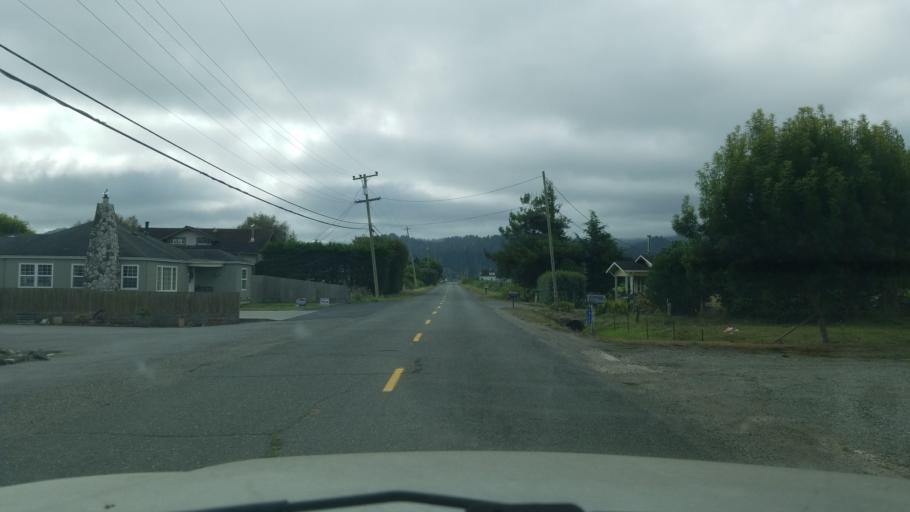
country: US
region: California
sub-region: Humboldt County
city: Ferndale
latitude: 40.5936
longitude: -124.2553
